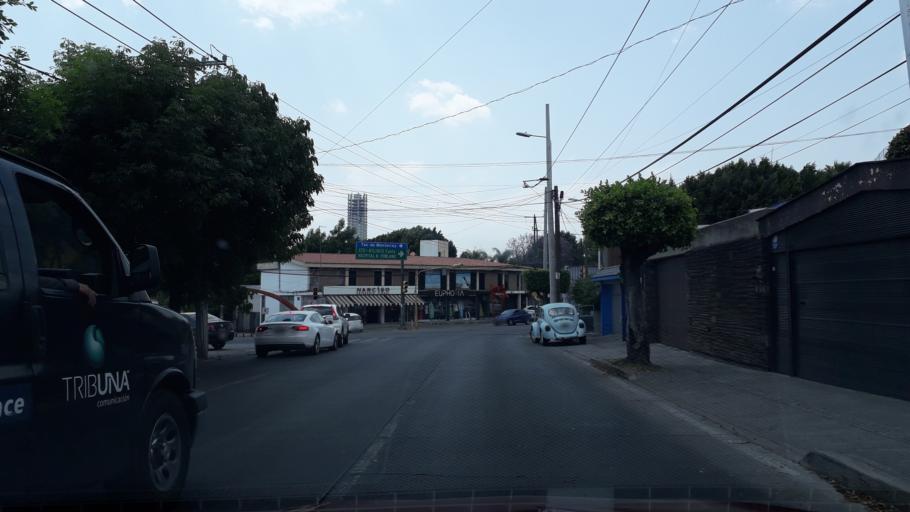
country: MX
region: Puebla
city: Puebla
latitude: 19.0303
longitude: -98.2221
